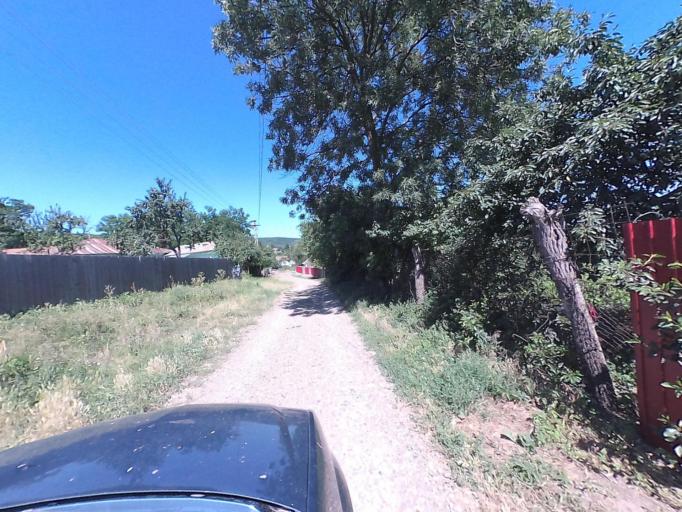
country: RO
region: Vaslui
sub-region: Comuna Costesti
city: Costesti
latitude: 46.4918
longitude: 27.7676
